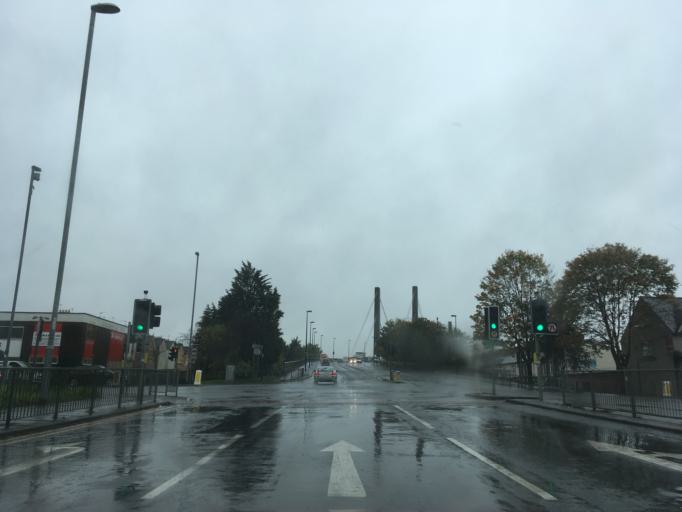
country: GB
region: Wales
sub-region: Newport
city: Newport
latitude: 51.5866
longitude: -2.9810
